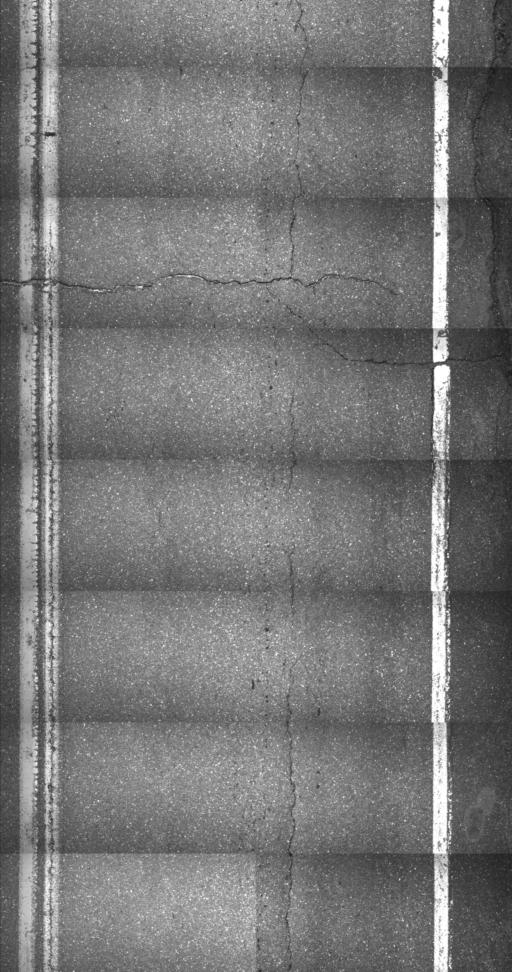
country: US
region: Vermont
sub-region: Caledonia County
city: Hardwick
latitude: 44.4510
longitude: -72.2548
